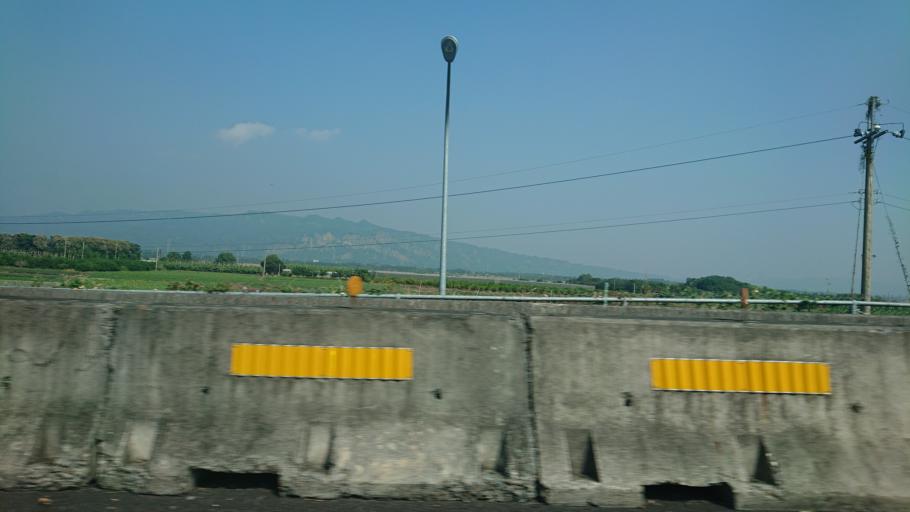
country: TW
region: Taiwan
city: Lugu
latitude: 23.7749
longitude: 120.6602
